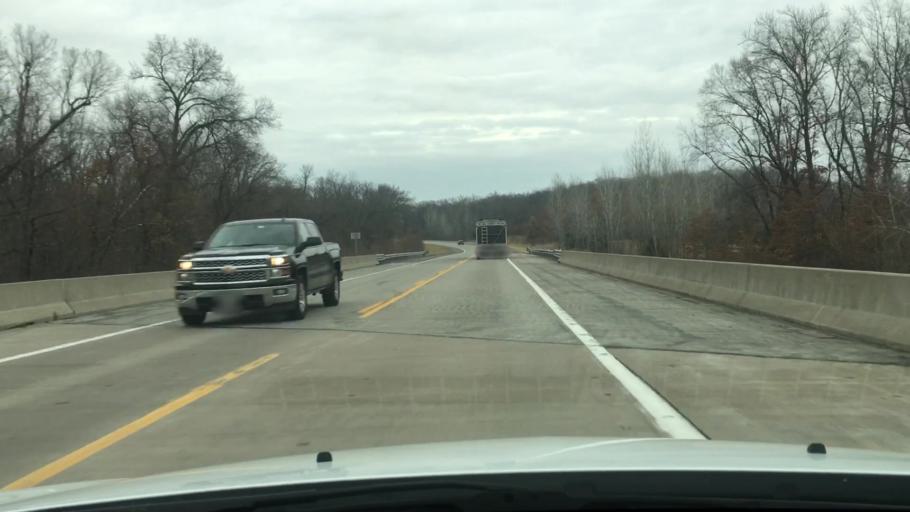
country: US
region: Missouri
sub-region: Audrain County
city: Mexico
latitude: 39.1434
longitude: -91.8468
